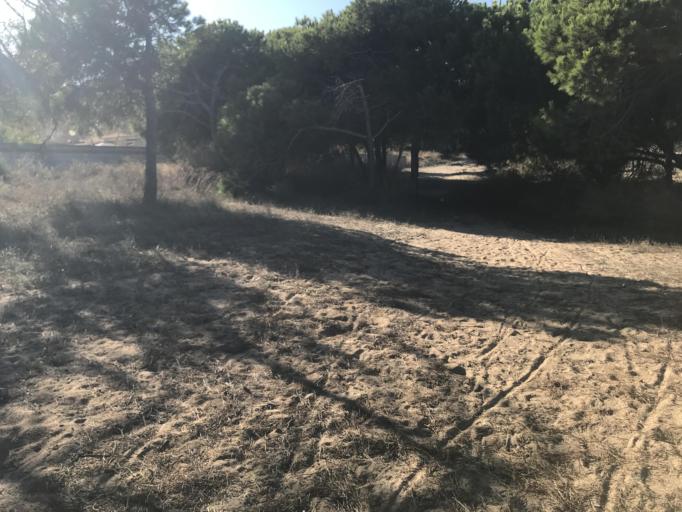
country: ES
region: Valencia
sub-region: Provincia de Alicante
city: Torrevieja
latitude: 38.0313
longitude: -0.6556
